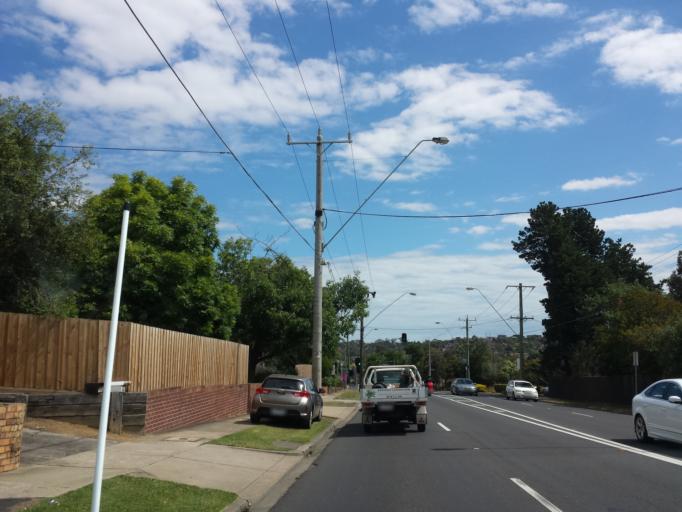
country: AU
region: Victoria
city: Rosanna
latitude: -37.7421
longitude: 145.0730
